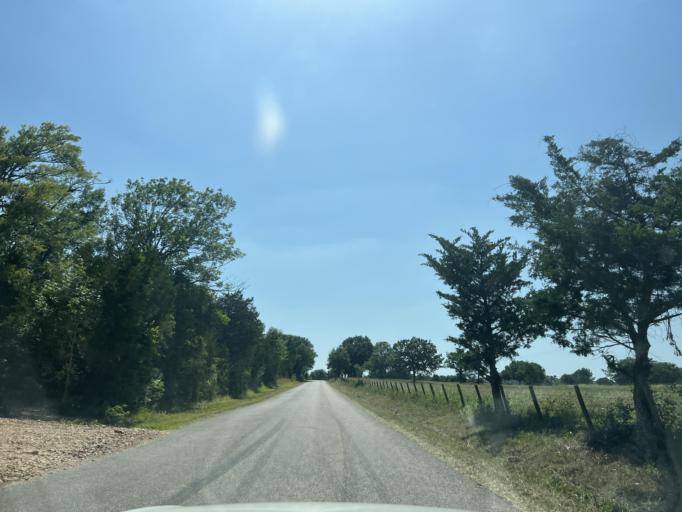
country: US
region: Texas
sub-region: Washington County
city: Brenham
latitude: 30.1600
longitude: -96.4464
